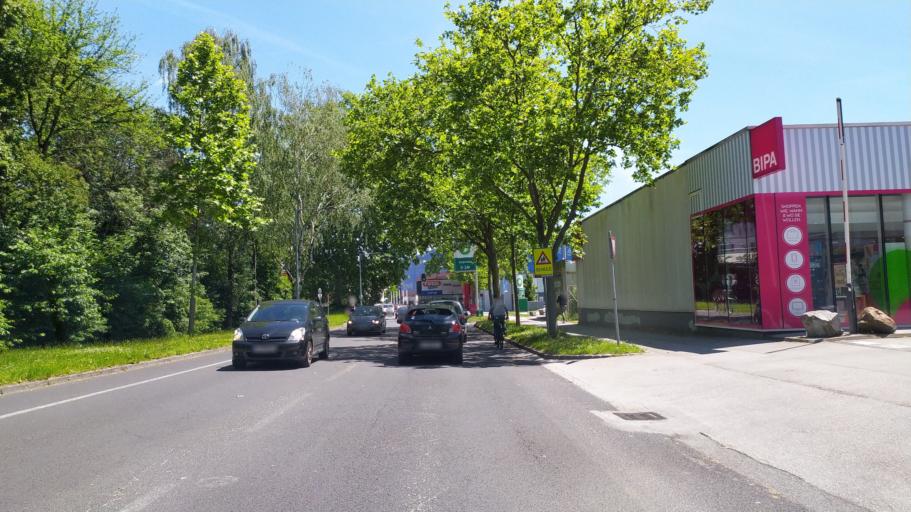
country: AT
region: Upper Austria
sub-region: Politischer Bezirk Linz-Land
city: Ansfelden
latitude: 48.2535
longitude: 14.3097
